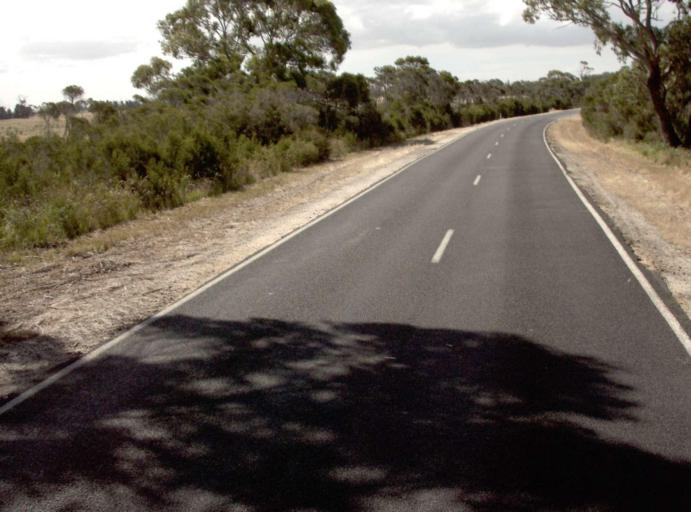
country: AU
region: Victoria
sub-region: Wellington
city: Sale
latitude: -38.3194
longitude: 147.1570
